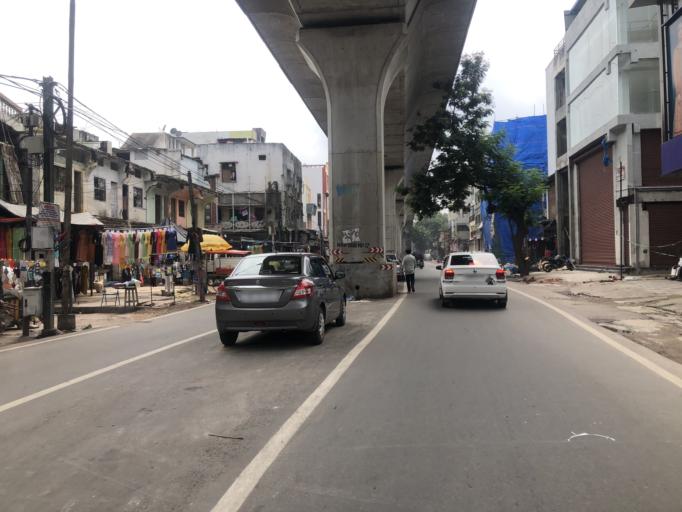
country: IN
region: Telangana
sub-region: Hyderabad
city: Hyderabad
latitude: 17.3897
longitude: 78.4885
